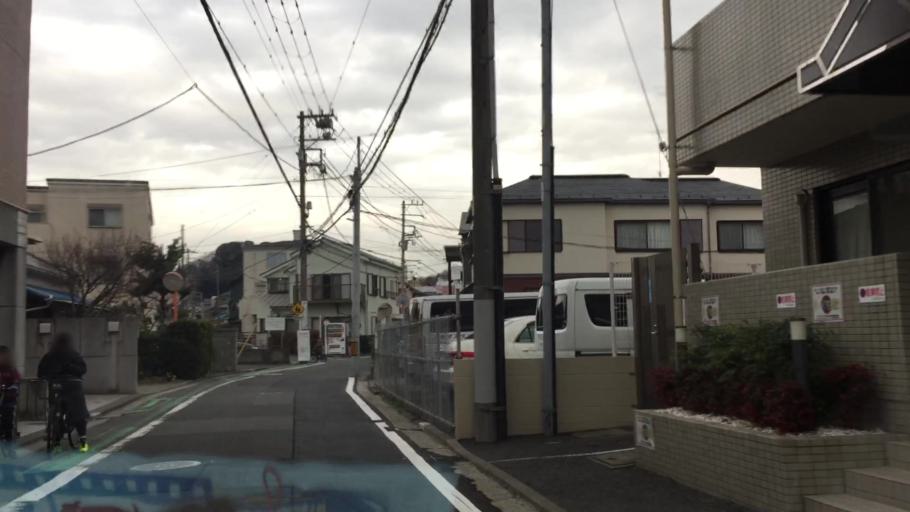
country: JP
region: Kanagawa
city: Yokosuka
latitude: 35.3389
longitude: 139.6280
